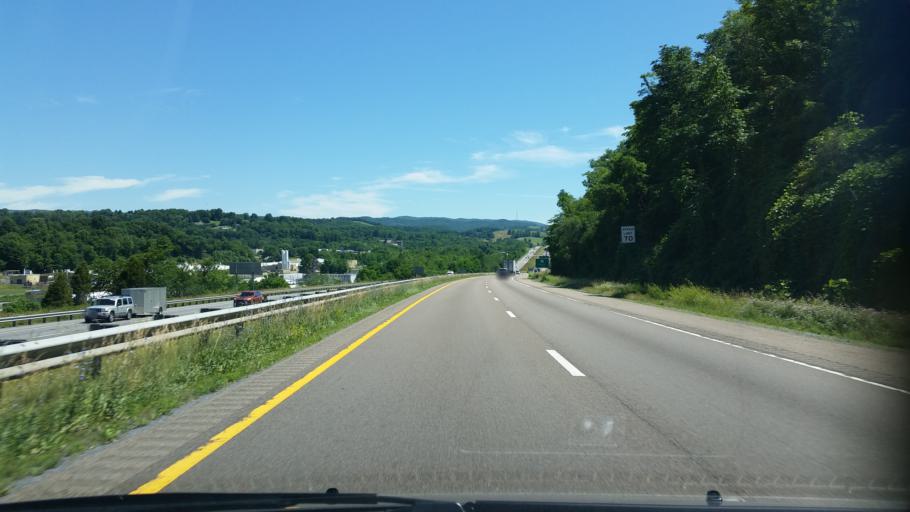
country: US
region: Virginia
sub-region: Smyth County
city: Marion
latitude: 36.8360
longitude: -81.4982
